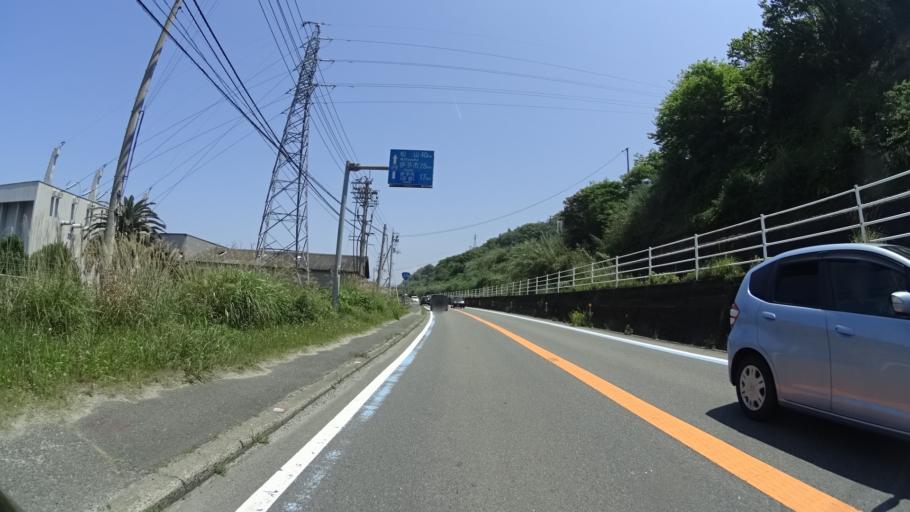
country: JP
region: Ehime
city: Ozu
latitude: 33.6180
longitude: 132.4943
